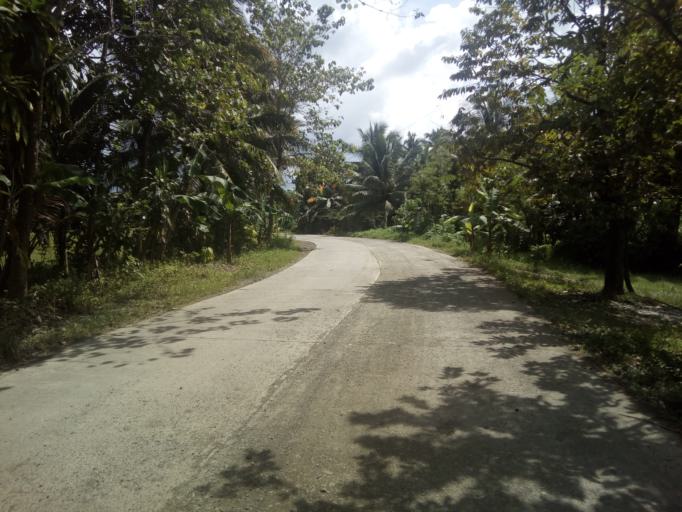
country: PH
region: Caraga
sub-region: Province of Agusan del Sur
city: Santa Josefa
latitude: 7.9905
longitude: 126.0324
